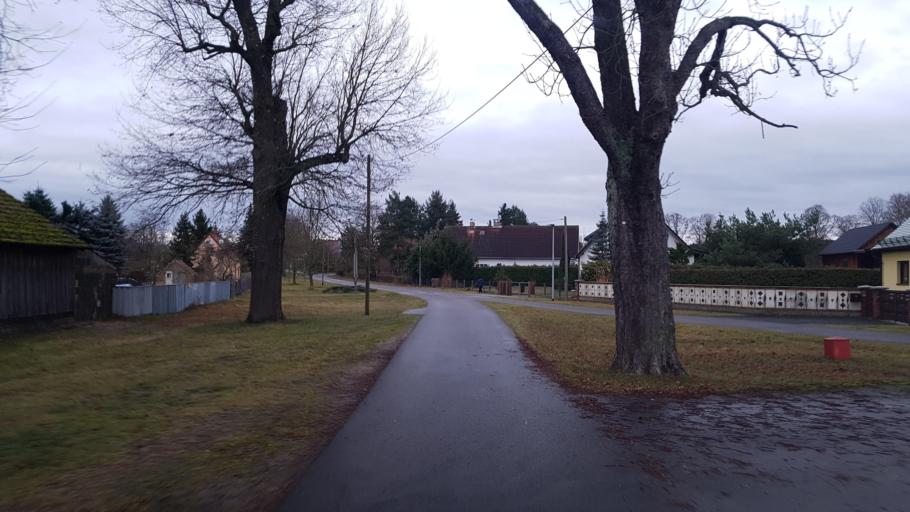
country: DE
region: Brandenburg
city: Tauche
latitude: 52.0695
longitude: 14.0975
